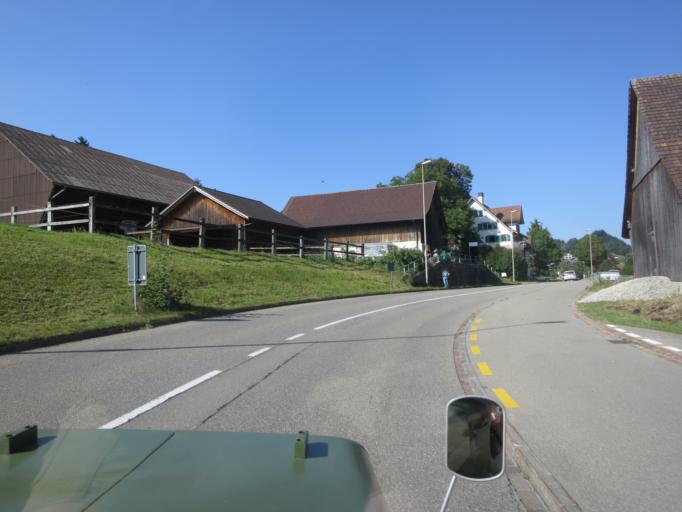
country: CH
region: Zurich
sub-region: Bezirk Hinwil
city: Wald
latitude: 47.3089
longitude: 8.9123
